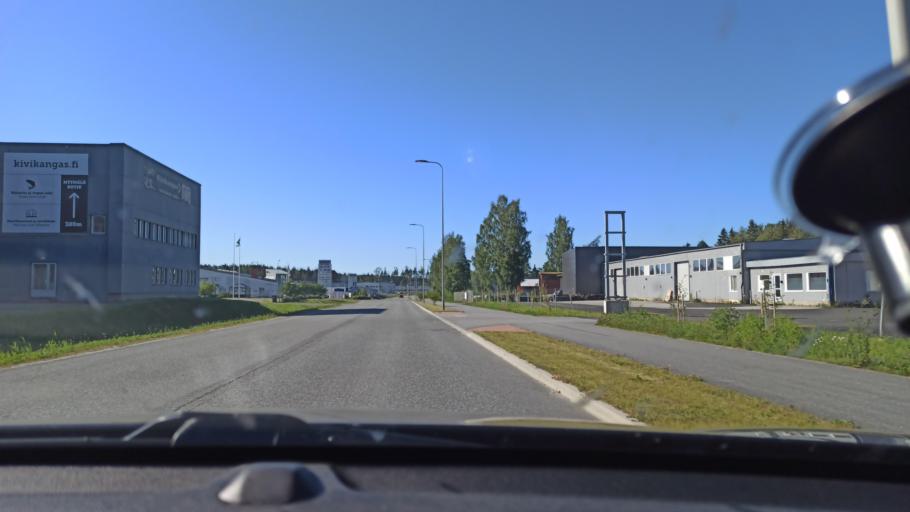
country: FI
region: Ostrobothnia
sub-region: Jakobstadsregionen
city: Jakobstad
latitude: 63.6863
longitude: 22.7098
